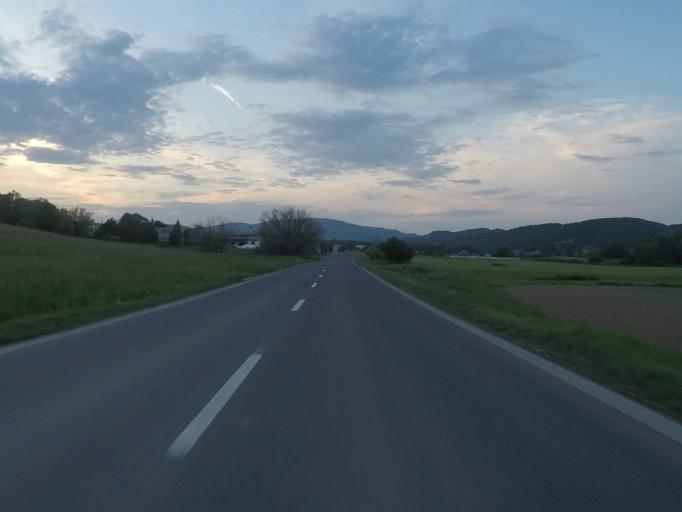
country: SK
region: Banskobystricky
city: Rimavska Sobota
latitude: 48.4561
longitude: 19.9540
